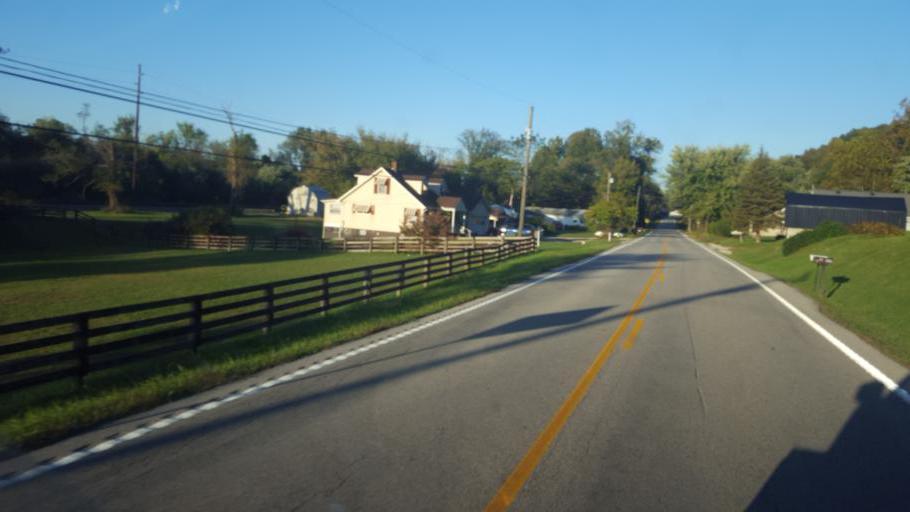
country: US
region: Ohio
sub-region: Scioto County
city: West Portsmouth
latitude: 38.6829
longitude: -83.0665
